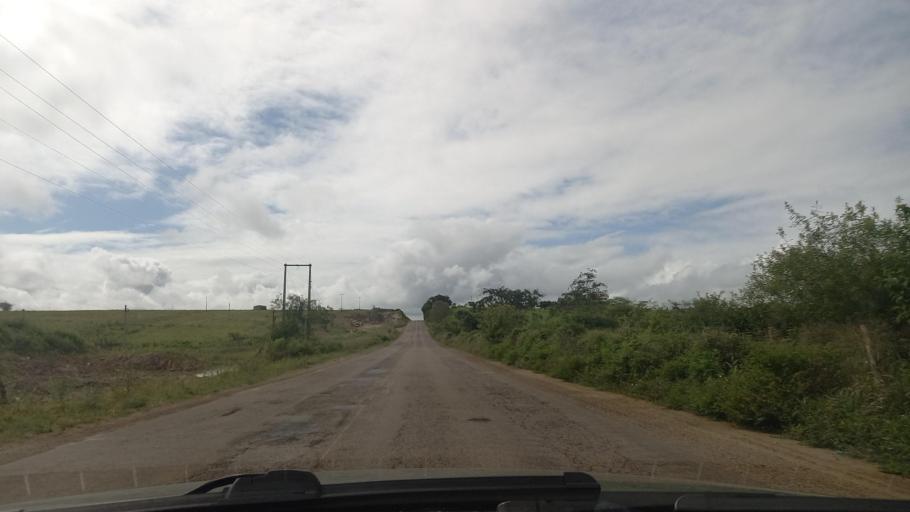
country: BR
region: Alagoas
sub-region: Batalha
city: Batalha
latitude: -9.6641
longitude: -37.1654
